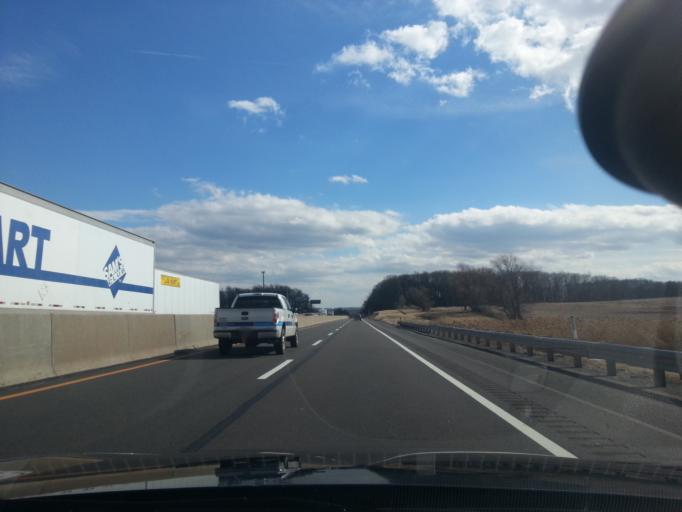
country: US
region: Pennsylvania
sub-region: Montgomery County
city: Harleysville
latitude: 40.2851
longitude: -75.3634
